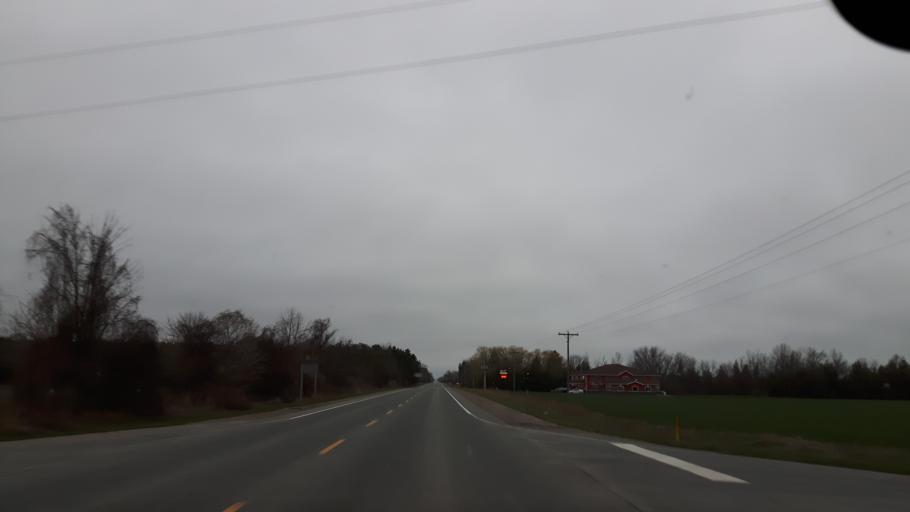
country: CA
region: Ontario
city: Goderich
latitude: 43.6799
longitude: -81.7057
